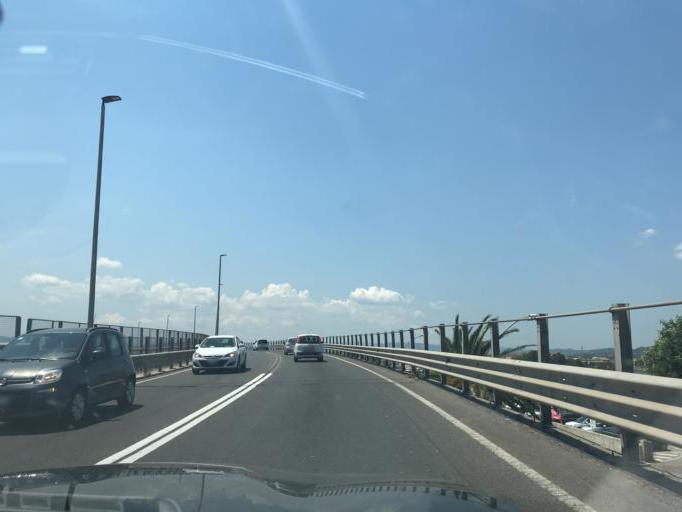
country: IT
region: Sardinia
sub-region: Provincia di Olbia-Tempio
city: Olbia
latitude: 40.9206
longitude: 9.5019
